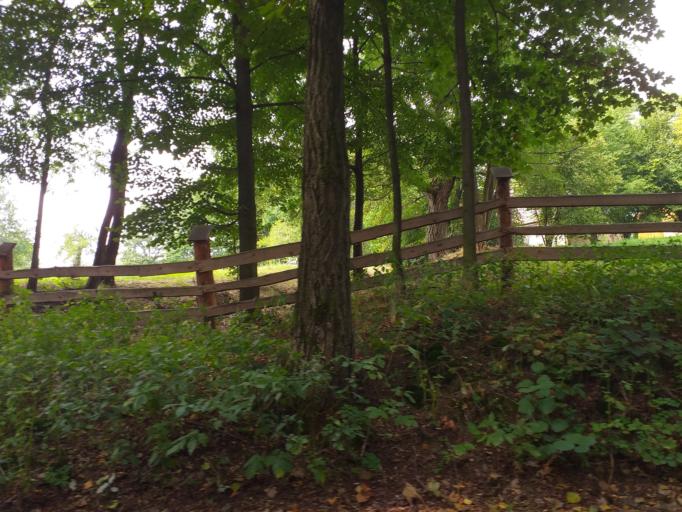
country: PL
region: Lower Silesian Voivodeship
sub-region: Powiat lubanski
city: Lesna
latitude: 51.0143
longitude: 15.3100
